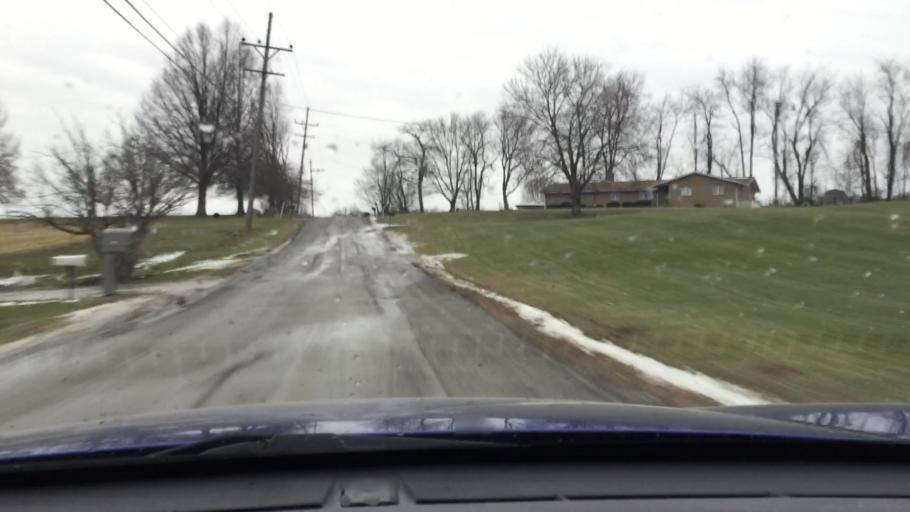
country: US
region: Pennsylvania
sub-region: Westmoreland County
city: Fellsburg
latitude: 40.1602
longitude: -79.8267
